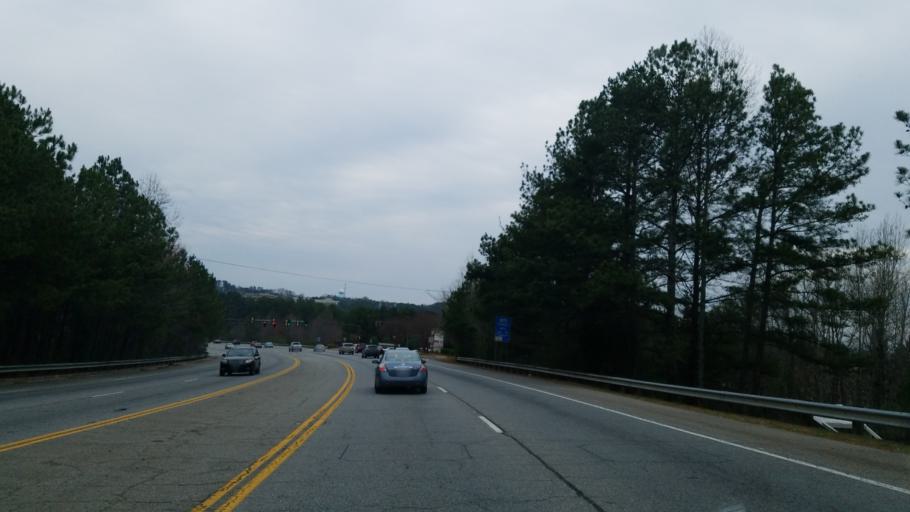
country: US
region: Georgia
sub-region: Cherokee County
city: Holly Springs
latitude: 34.1935
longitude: -84.5093
